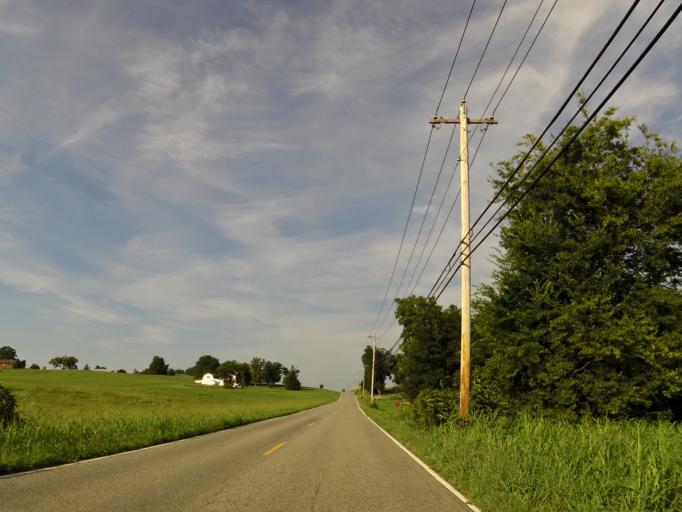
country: US
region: Tennessee
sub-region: Blount County
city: Wildwood
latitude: 35.8227
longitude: -83.8163
